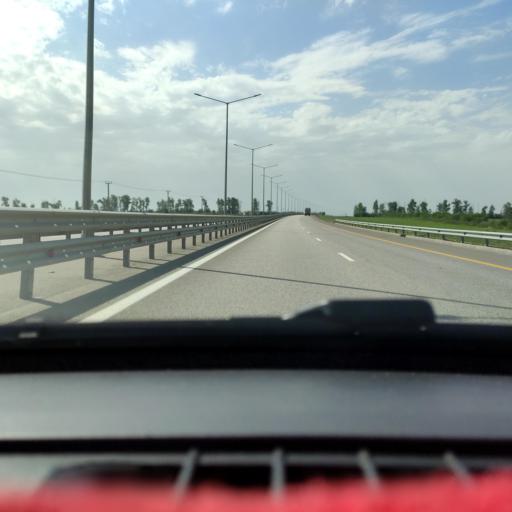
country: RU
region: Voronezj
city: Podkletnoye
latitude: 51.5289
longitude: 39.5091
